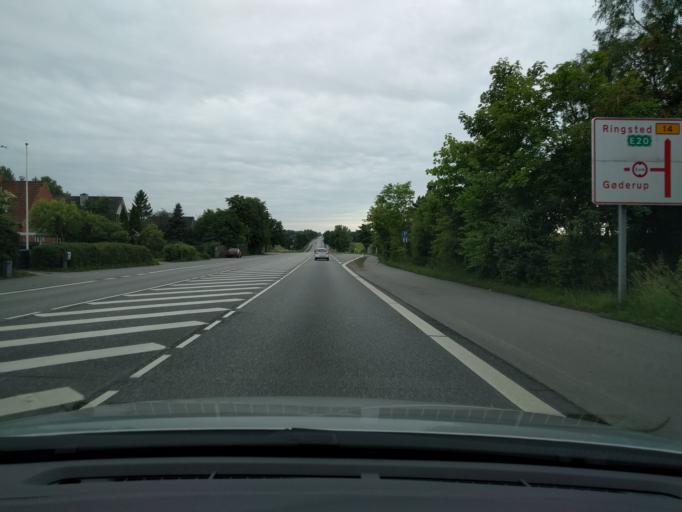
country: DK
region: Zealand
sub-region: Roskilde Kommune
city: Svogerslev
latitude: 55.6011
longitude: 12.0239
